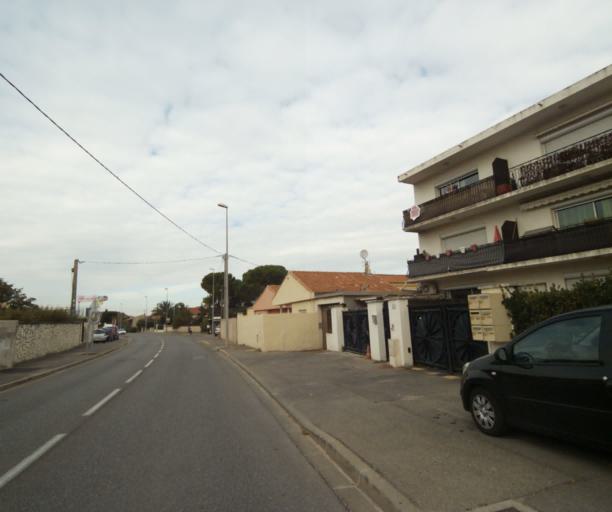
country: FR
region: Provence-Alpes-Cote d'Azur
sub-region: Departement des Bouches-du-Rhone
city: Saint-Victoret
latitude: 43.4194
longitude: 5.2424
